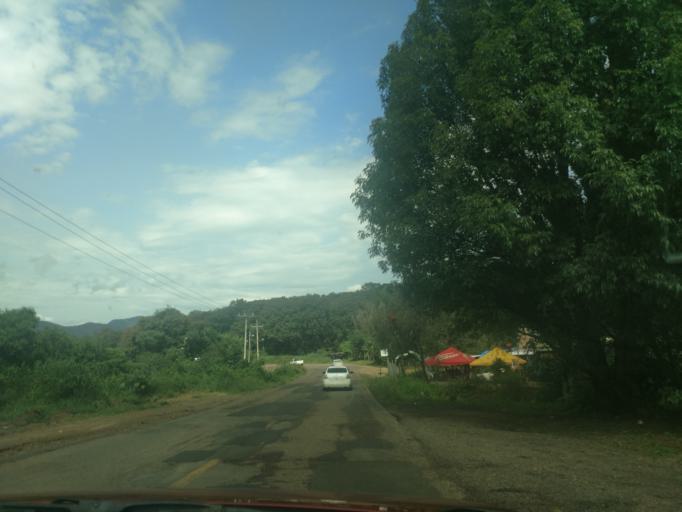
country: MX
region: Jalisco
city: Talpa de Allende
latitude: 20.4246
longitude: -104.7321
